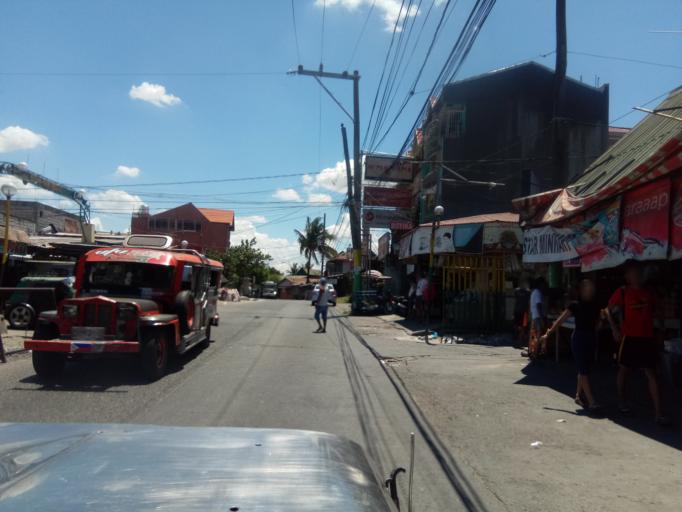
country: PH
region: Calabarzon
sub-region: Province of Cavite
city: Dasmarinas
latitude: 14.3245
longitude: 120.9683
